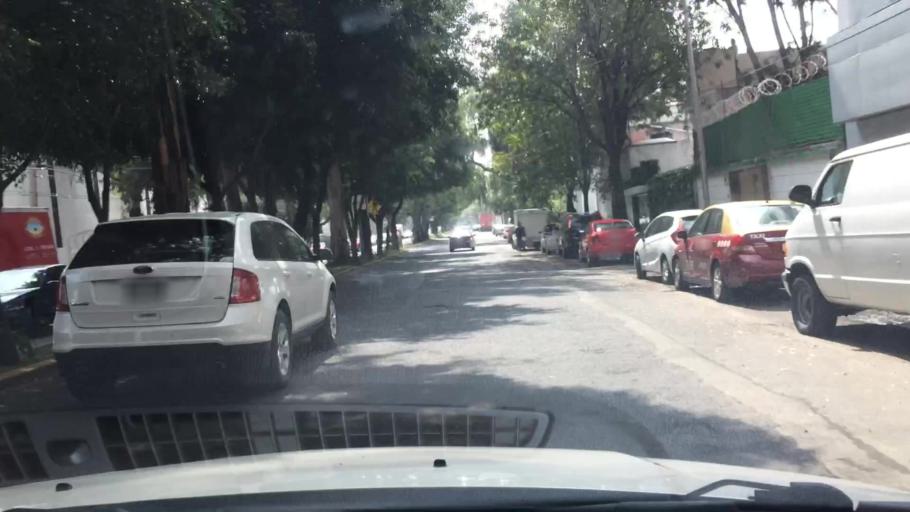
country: MX
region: Mexico City
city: Coyoacan
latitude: 19.3427
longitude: -99.1555
